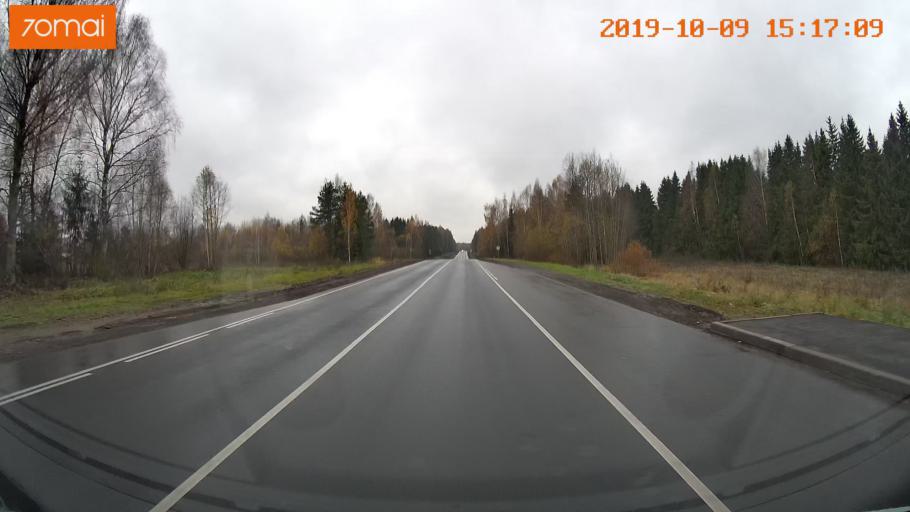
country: RU
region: Kostroma
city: Susanino
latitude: 58.1020
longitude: 41.5838
